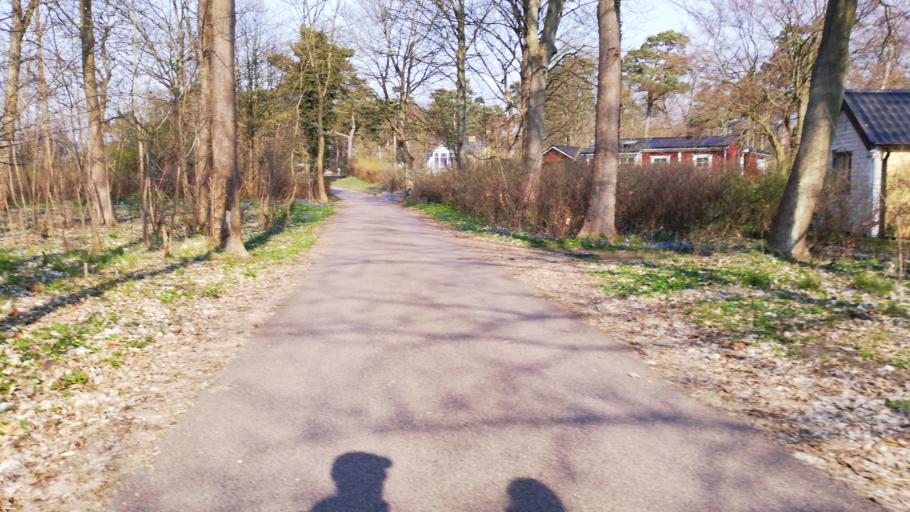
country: SE
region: Skane
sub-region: Ystads Kommun
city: Ystad
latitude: 55.4269
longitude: 13.8439
